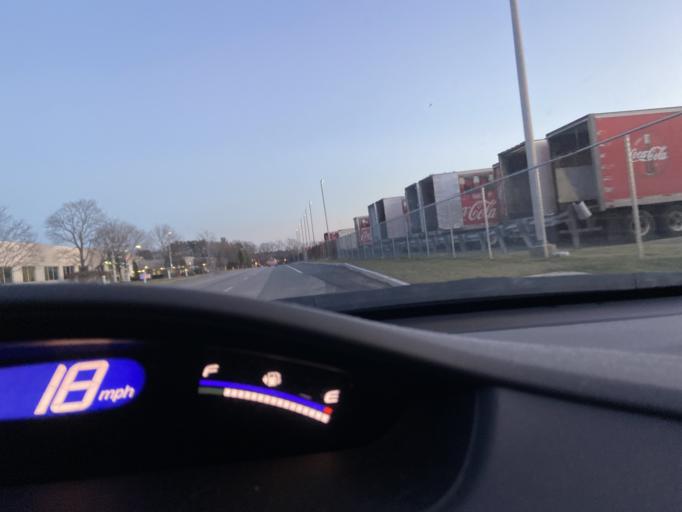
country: US
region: Massachusetts
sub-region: Norfolk County
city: Needham
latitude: 42.2985
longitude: -71.2159
